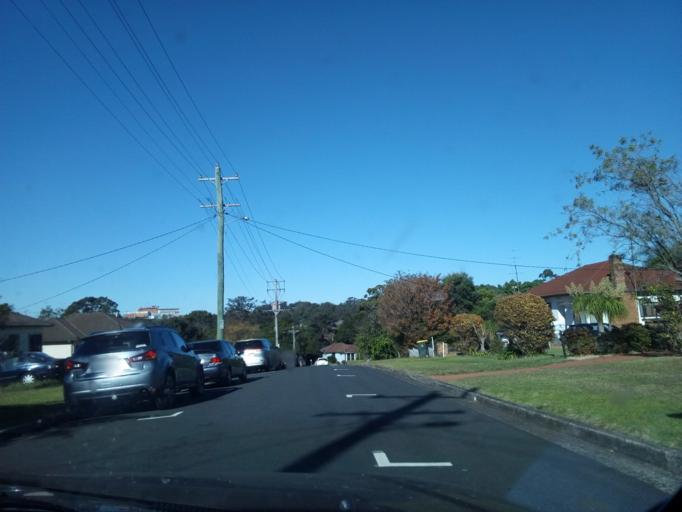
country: AU
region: New South Wales
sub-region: Wollongong
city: Gwynneville
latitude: -34.4103
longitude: 150.8812
